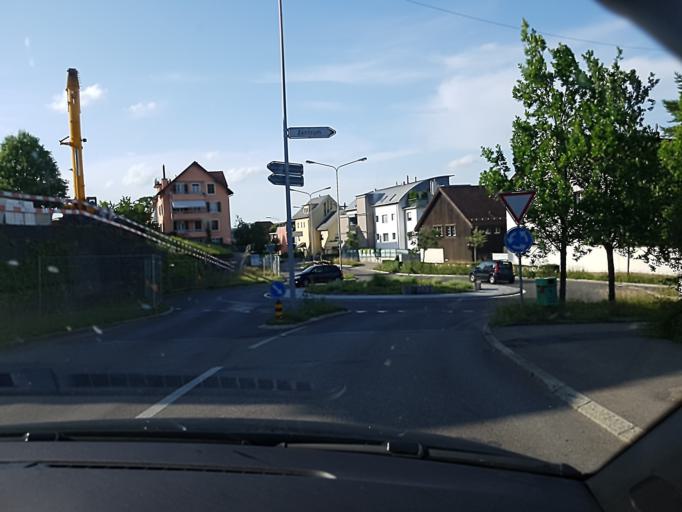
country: CH
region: Zurich
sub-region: Bezirk Horgen
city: Thalwil / Nord
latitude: 47.2976
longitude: 8.5597
